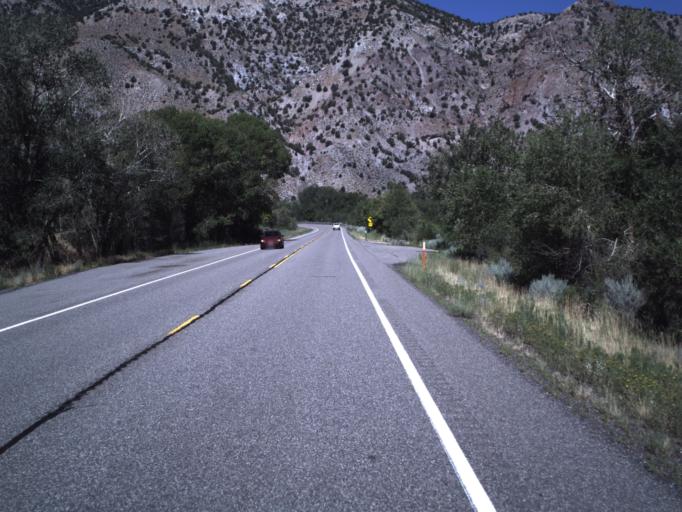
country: US
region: Utah
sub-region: Sevier County
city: Monroe
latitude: 38.5687
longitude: -112.2612
